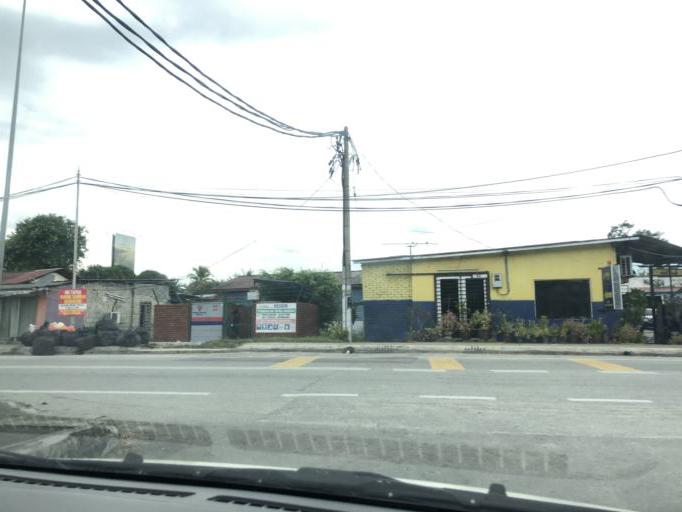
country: MY
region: Putrajaya
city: Putrajaya
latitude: 2.9214
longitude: 101.7583
